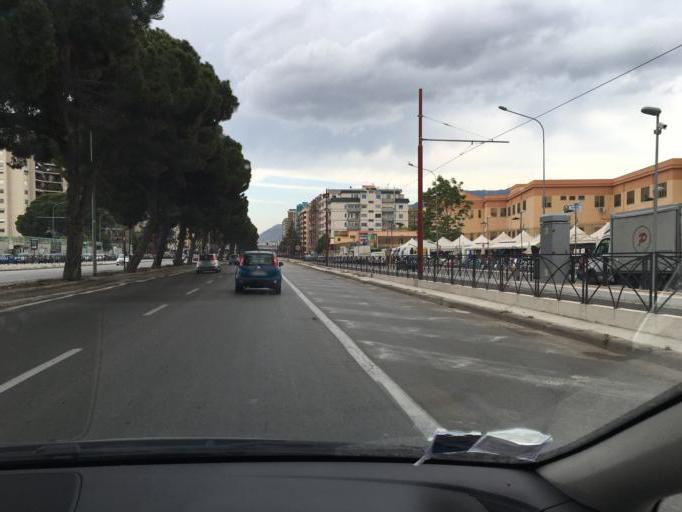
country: IT
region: Sicily
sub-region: Palermo
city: Palermo
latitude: 38.1207
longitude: 13.3289
